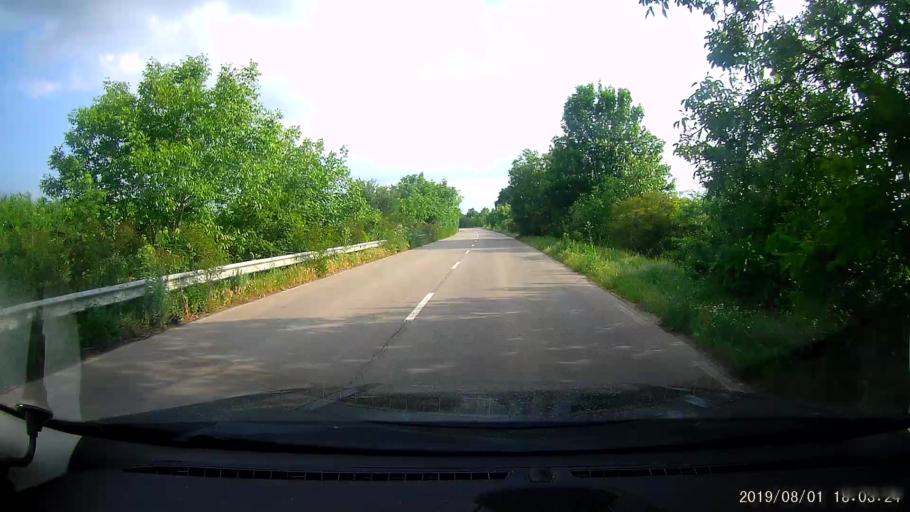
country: BG
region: Silistra
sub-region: Obshtina Alfatar
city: Alfatar
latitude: 43.9283
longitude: 27.2892
